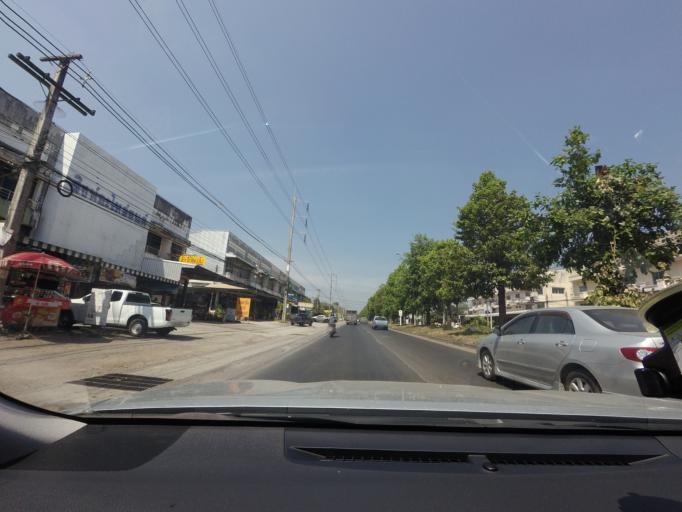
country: TH
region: Surat Thani
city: Kanchanadit
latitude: 9.1628
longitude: 99.4757
